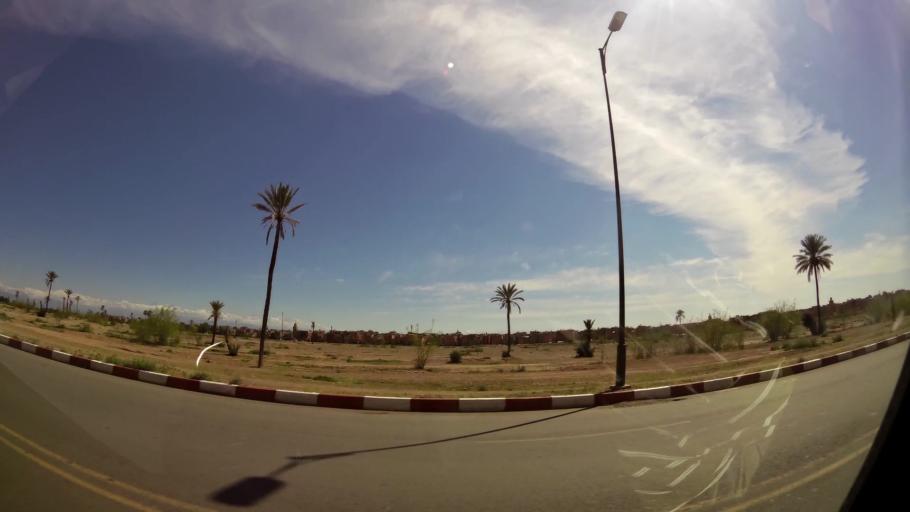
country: MA
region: Marrakech-Tensift-Al Haouz
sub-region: Marrakech
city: Marrakesh
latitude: 31.6201
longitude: -7.9623
